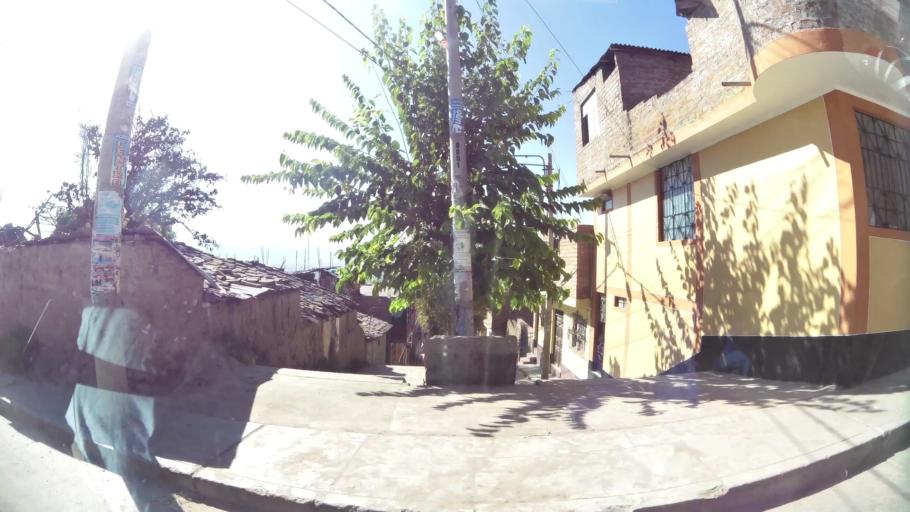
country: PE
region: Ayacucho
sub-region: Provincia de Huamanga
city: Ayacucho
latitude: -13.1634
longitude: -74.2313
